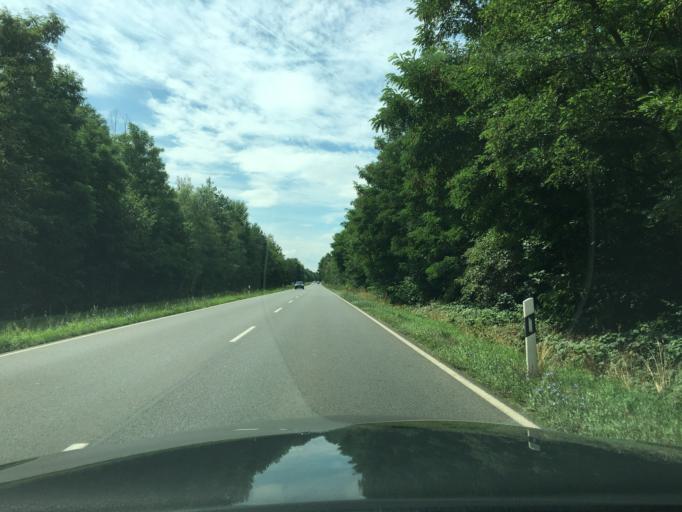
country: DE
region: Saxony-Anhalt
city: Roitzsch
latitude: 51.5908
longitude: 12.2658
